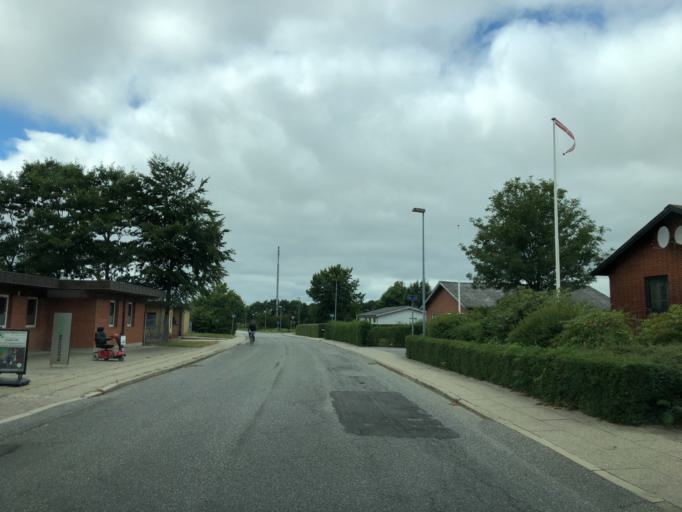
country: DK
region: Central Jutland
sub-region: Herning Kommune
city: Vildbjerg
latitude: 56.1968
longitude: 8.7618
